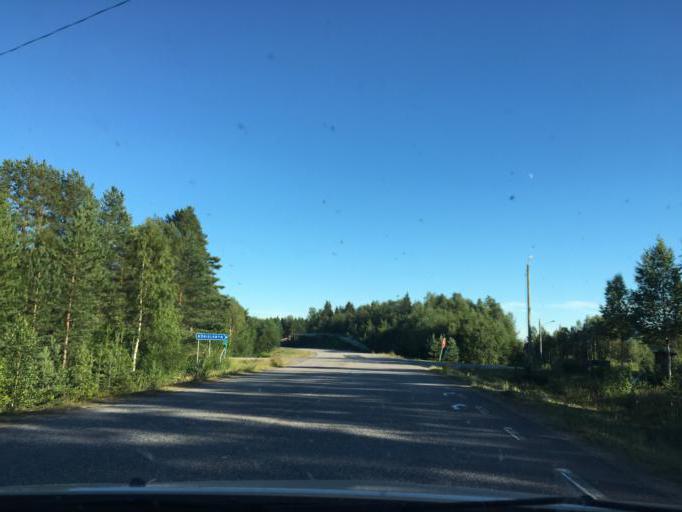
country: SE
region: Norrbotten
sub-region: Kalix Kommun
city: Rolfs
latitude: 65.9054
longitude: 22.9303
